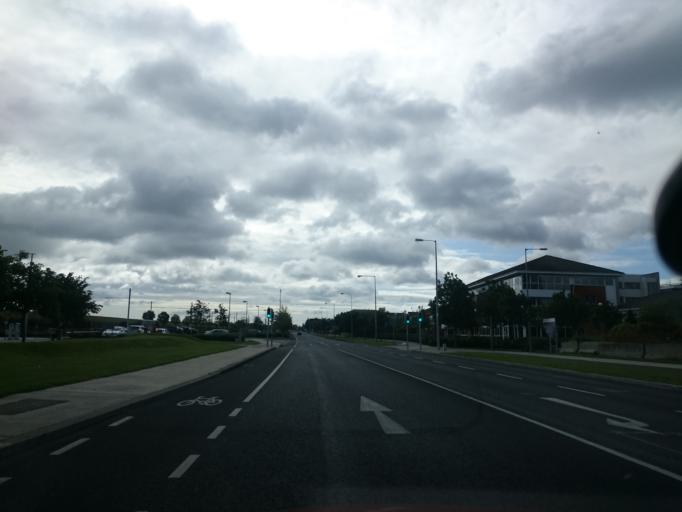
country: IE
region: Leinster
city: Sandyford
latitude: 53.2792
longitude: -6.2107
